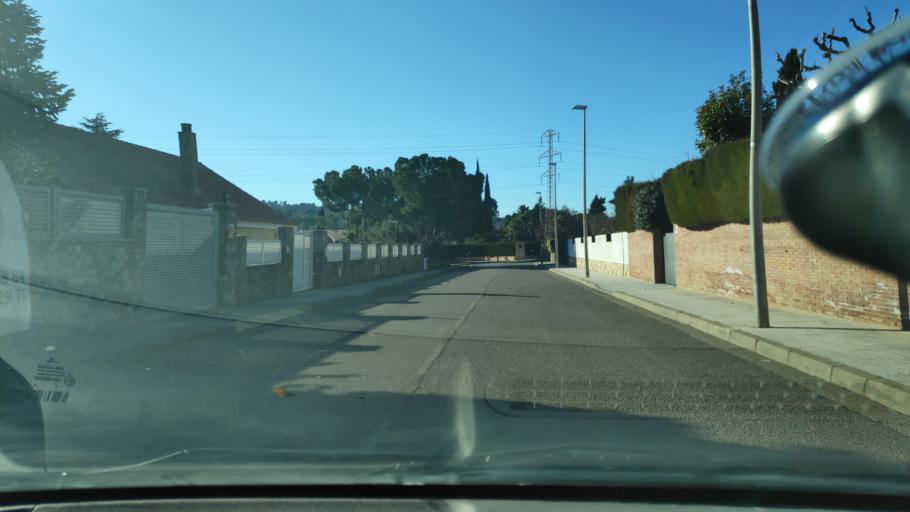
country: ES
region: Catalonia
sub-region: Provincia de Barcelona
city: Sant Quirze del Valles
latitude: 41.5386
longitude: 2.0662
